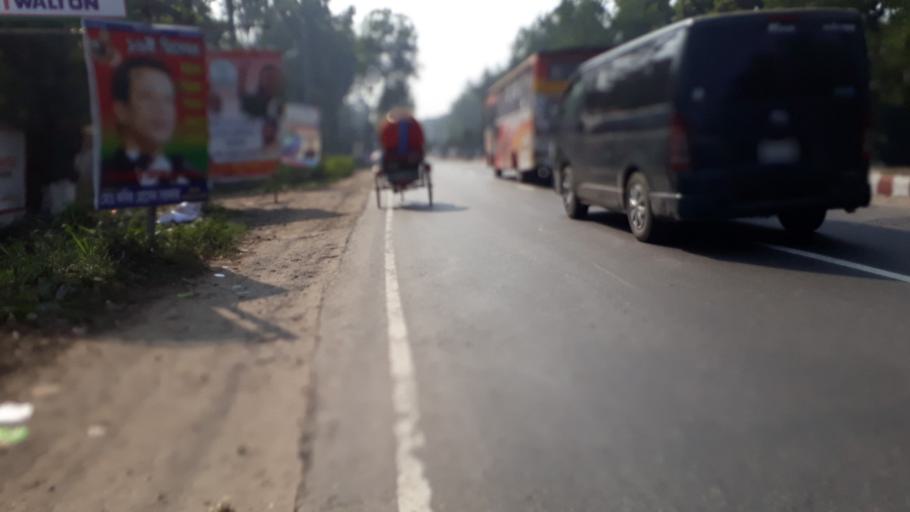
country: BD
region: Dhaka
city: Tungi
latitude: 23.8745
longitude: 90.2735
